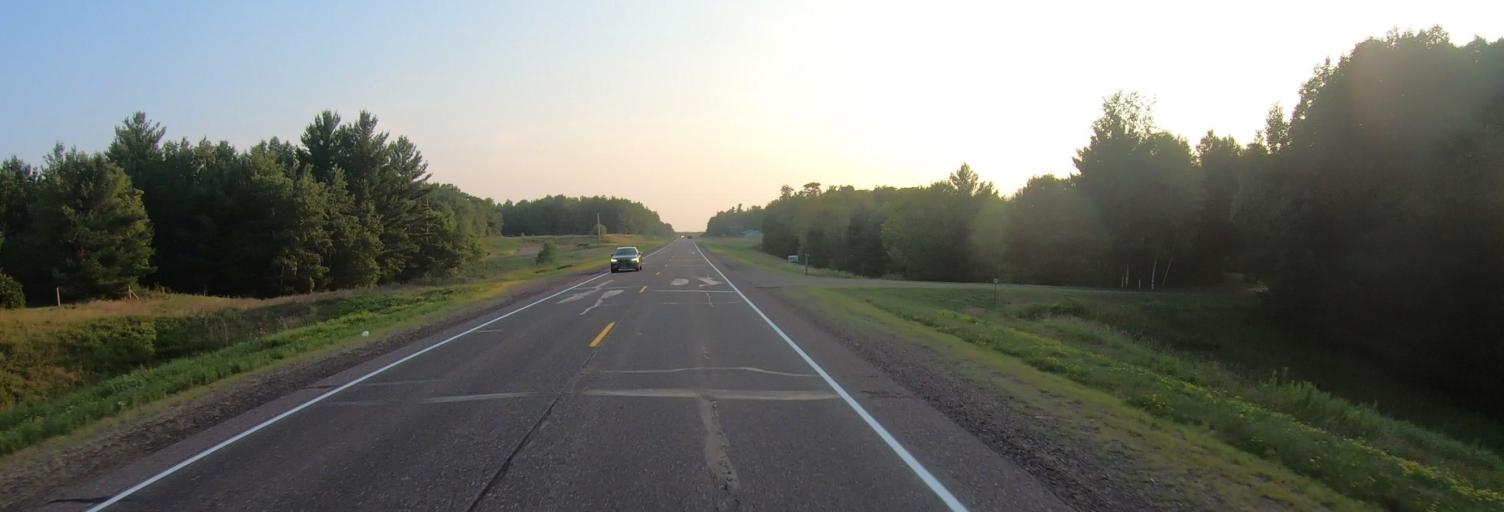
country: US
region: Wisconsin
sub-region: Burnett County
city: Siren
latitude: 45.7724
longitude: -92.4557
